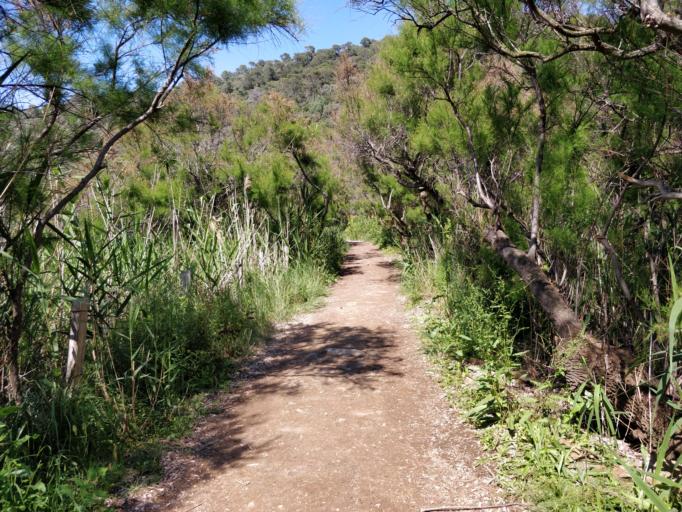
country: FR
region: Provence-Alpes-Cote d'Azur
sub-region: Departement du Var
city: Le Lavandou
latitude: 43.0067
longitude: 6.3832
